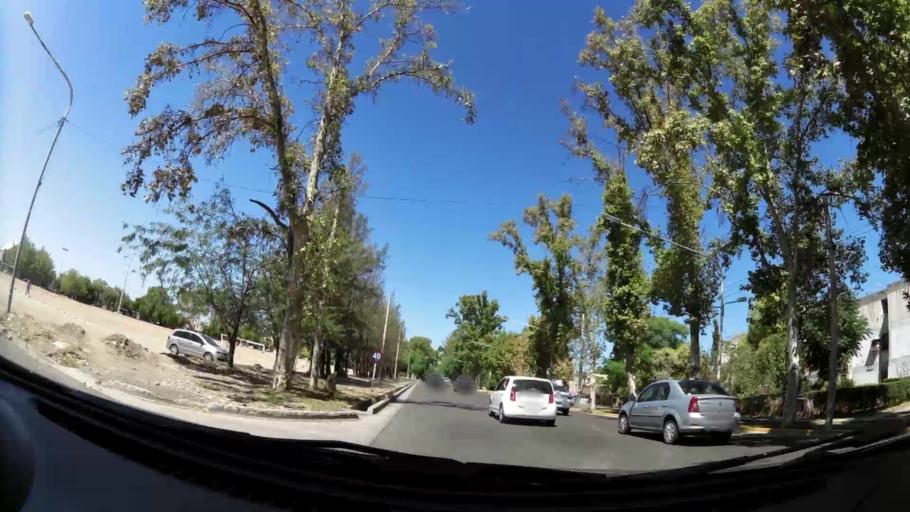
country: AR
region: Mendoza
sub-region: Departamento de Godoy Cruz
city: Godoy Cruz
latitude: -32.9050
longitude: -68.8670
